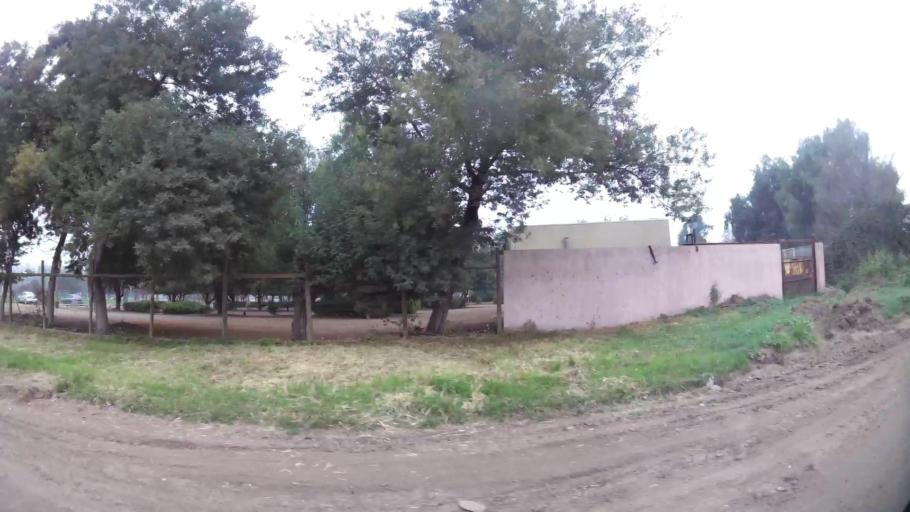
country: CL
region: Santiago Metropolitan
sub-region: Provincia de Chacabuco
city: Chicureo Abajo
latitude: -33.2274
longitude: -70.6757
